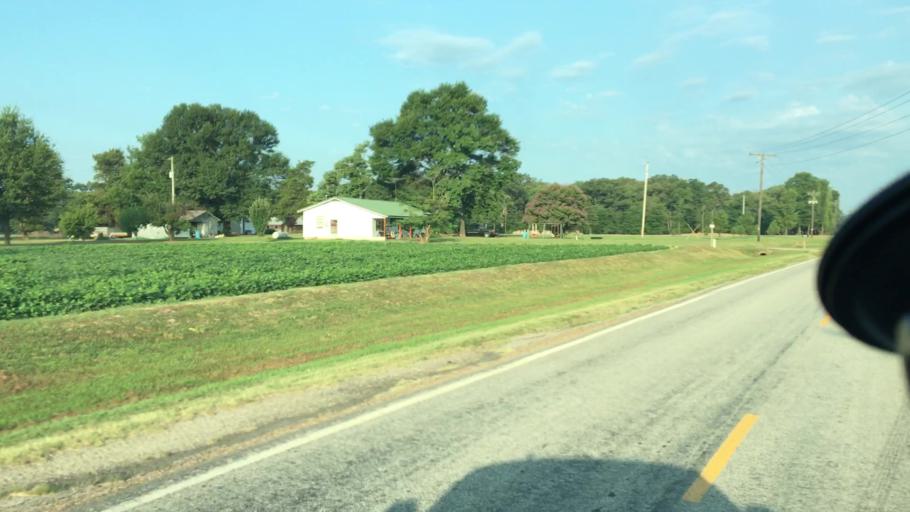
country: US
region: Arkansas
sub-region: Johnson County
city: Coal Hill
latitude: 35.3371
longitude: -93.6141
